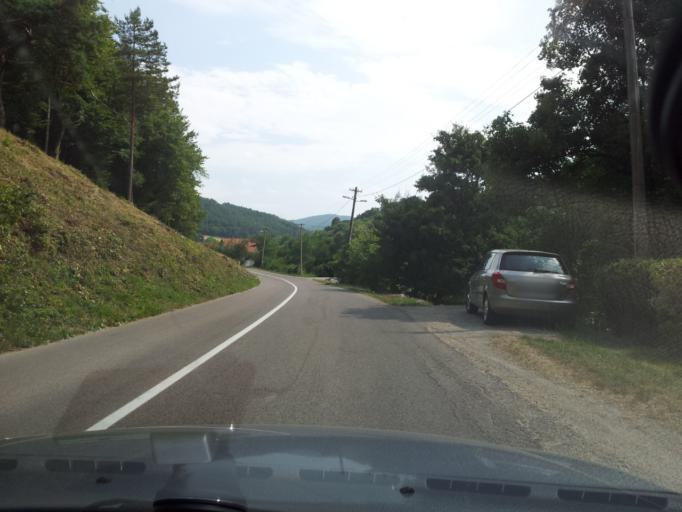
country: SK
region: Trenciansky
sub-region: Okres Trencin
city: Trencin
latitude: 48.8849
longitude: 18.0990
